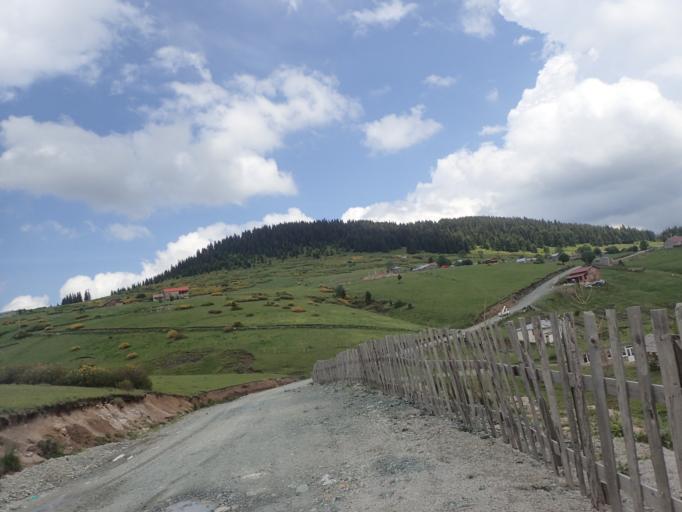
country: TR
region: Ordu
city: Topcam
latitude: 40.6837
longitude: 37.9430
